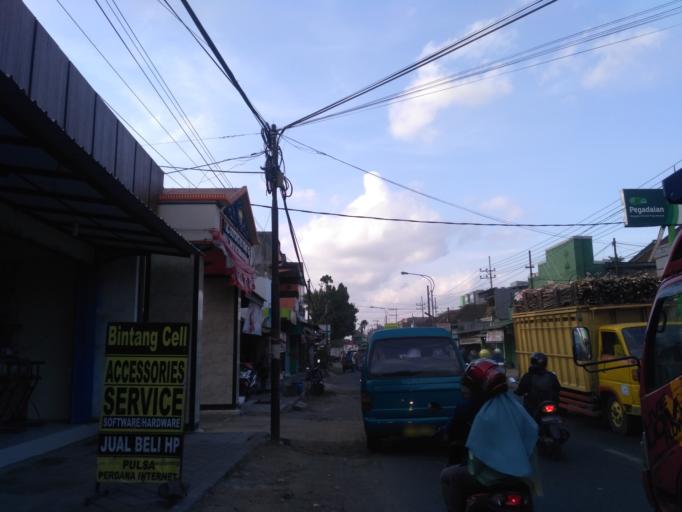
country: ID
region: East Java
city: Kebonsari
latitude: -8.0251
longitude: 112.6169
